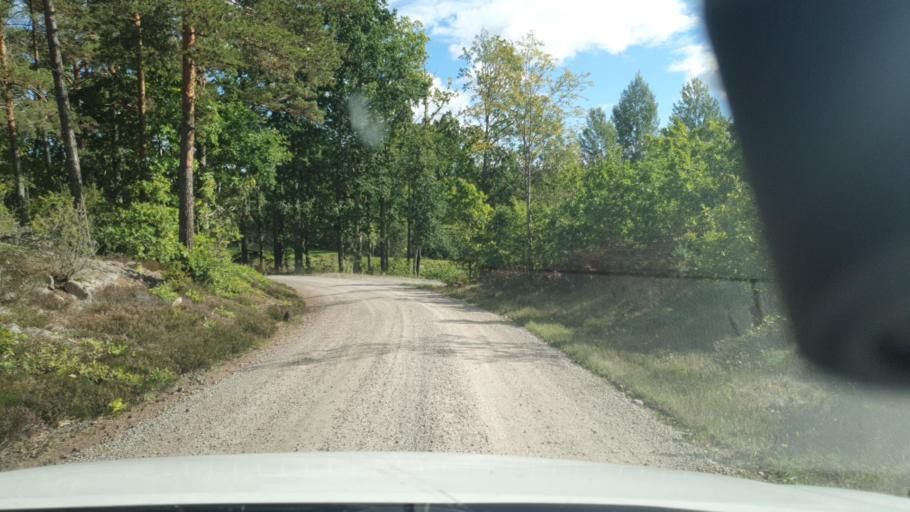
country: SE
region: Kalmar
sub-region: Vasterviks Kommun
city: Vaestervik
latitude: 57.7313
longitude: 16.4831
